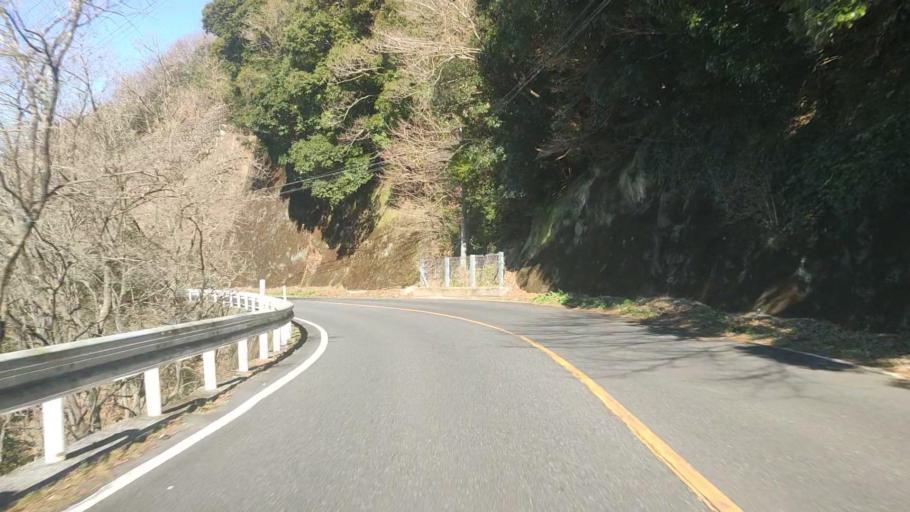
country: JP
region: Oita
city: Saiki
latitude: 32.8879
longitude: 131.9437
